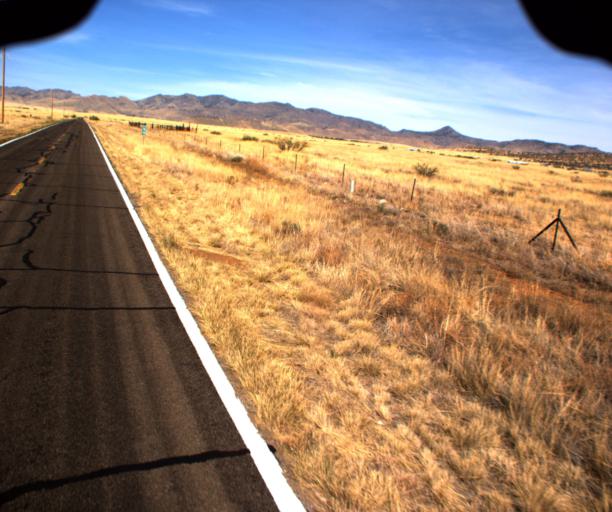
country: US
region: Arizona
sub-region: Cochise County
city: Willcox
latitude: 31.9857
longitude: -109.4558
